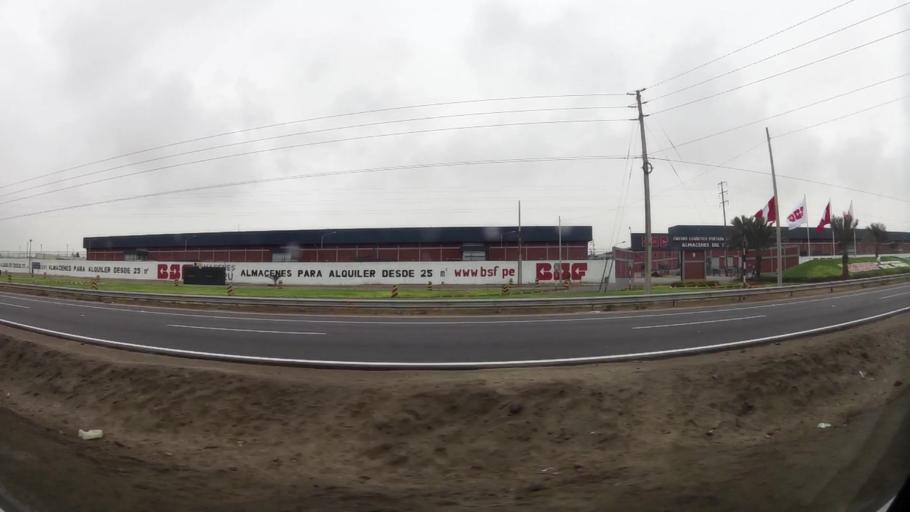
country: PE
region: Lima
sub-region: Lima
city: Punta Hermosa
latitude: -12.3178
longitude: -76.8303
